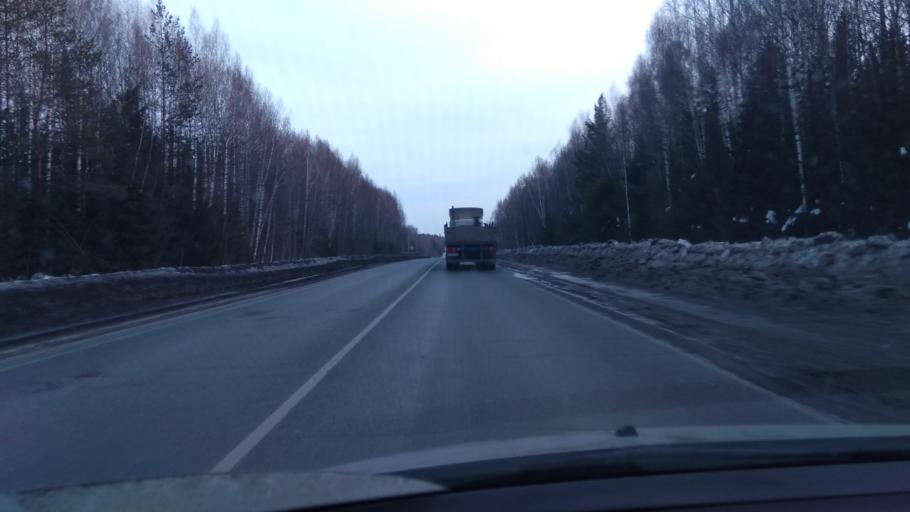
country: RU
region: Perm
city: Kukushtan
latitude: 57.5703
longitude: 56.5642
